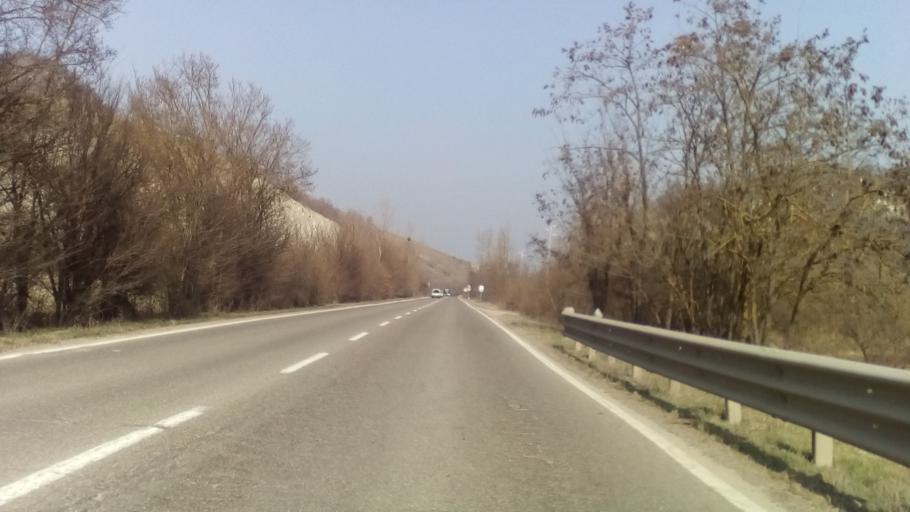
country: IT
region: Emilia-Romagna
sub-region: Provincia di Modena
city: Gorzano
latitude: 44.4742
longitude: 10.8481
